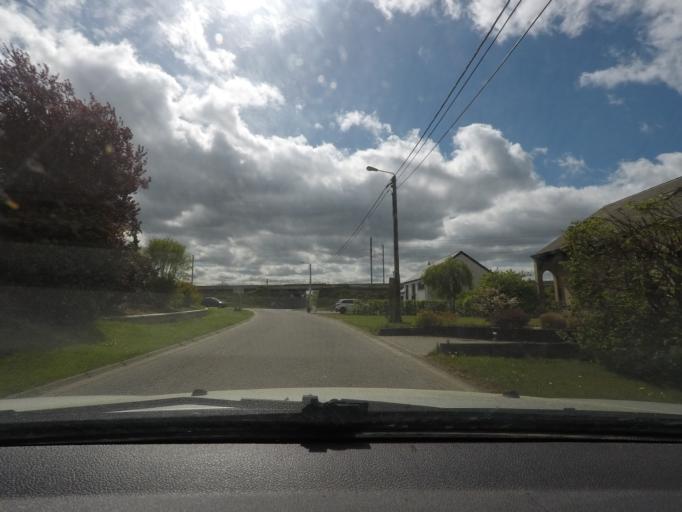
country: BE
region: Wallonia
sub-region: Province du Luxembourg
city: Habay-la-Vieille
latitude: 49.7209
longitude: 5.6158
